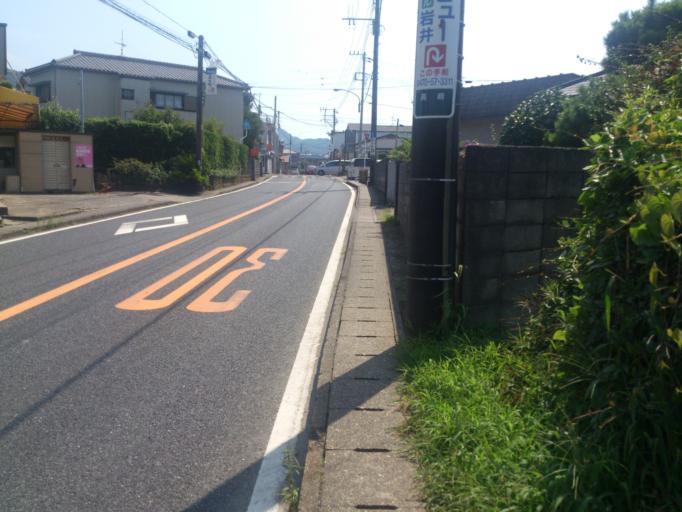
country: JP
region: Chiba
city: Tateyama
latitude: 35.0880
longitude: 139.8469
